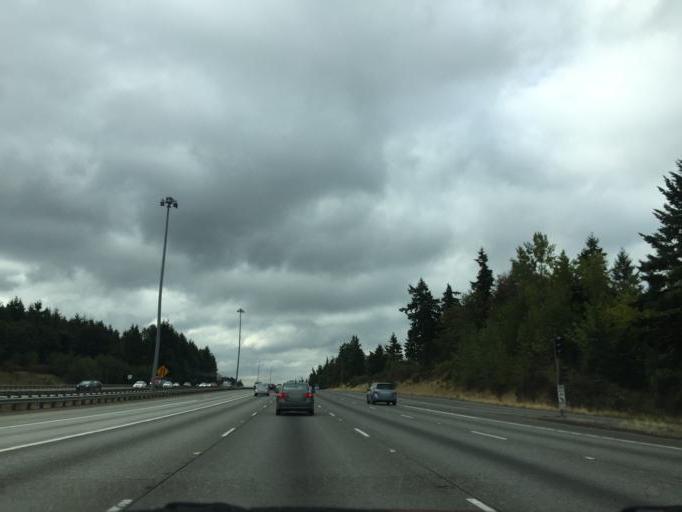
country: US
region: Washington
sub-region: King County
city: Federal Way
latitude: 47.3125
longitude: -122.2988
